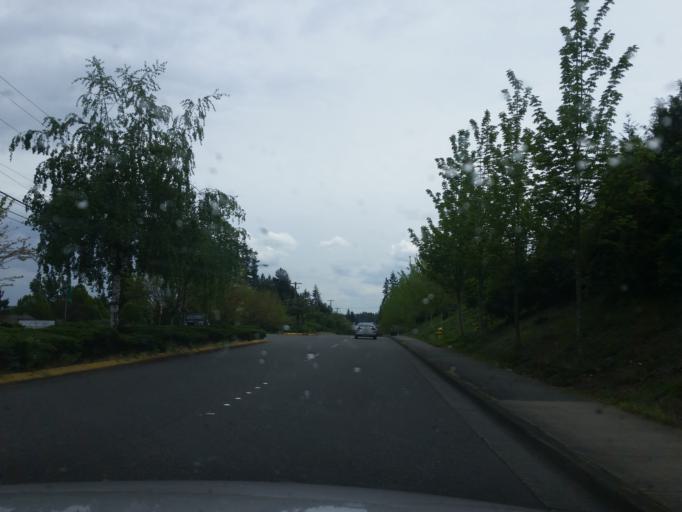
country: US
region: Washington
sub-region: Snohomish County
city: Alderwood Manor
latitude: 47.8313
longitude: -122.2819
